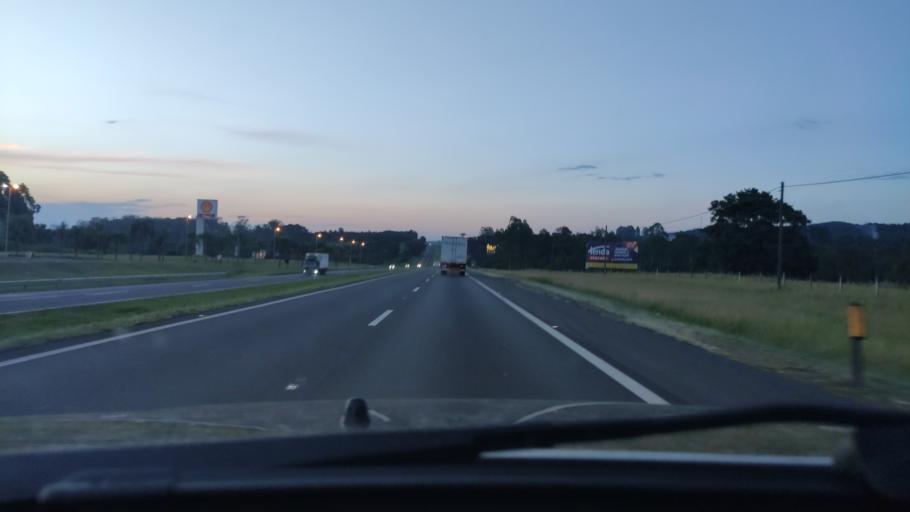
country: BR
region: Sao Paulo
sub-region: Sao Carlos
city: Sao Carlos
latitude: -22.0914
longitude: -47.8319
